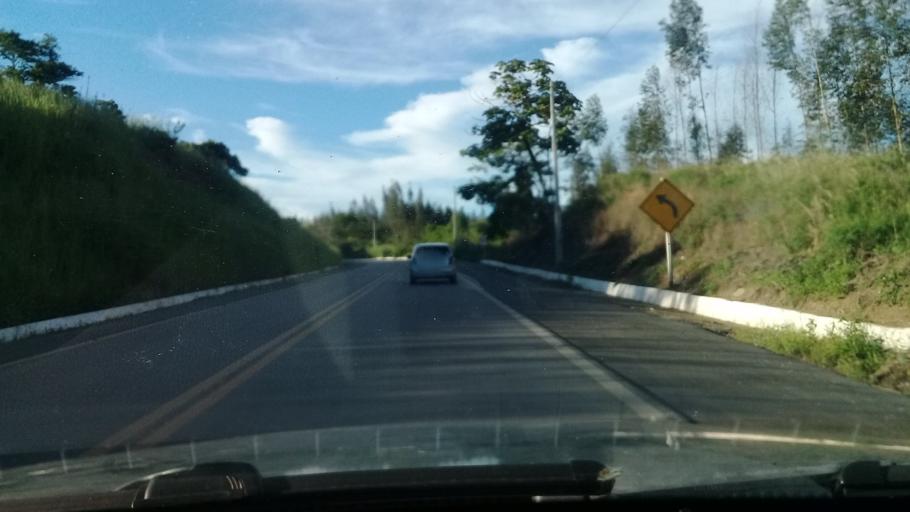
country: BR
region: Pernambuco
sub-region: Nazare Da Mata
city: Nazare da Mata
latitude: -7.7174
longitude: -35.2379
